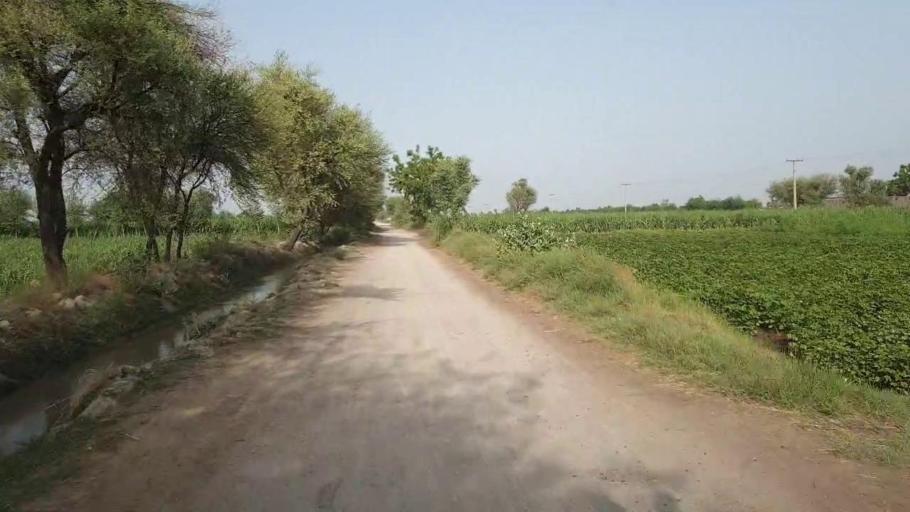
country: PK
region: Sindh
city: Daur
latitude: 26.3408
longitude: 68.1908
